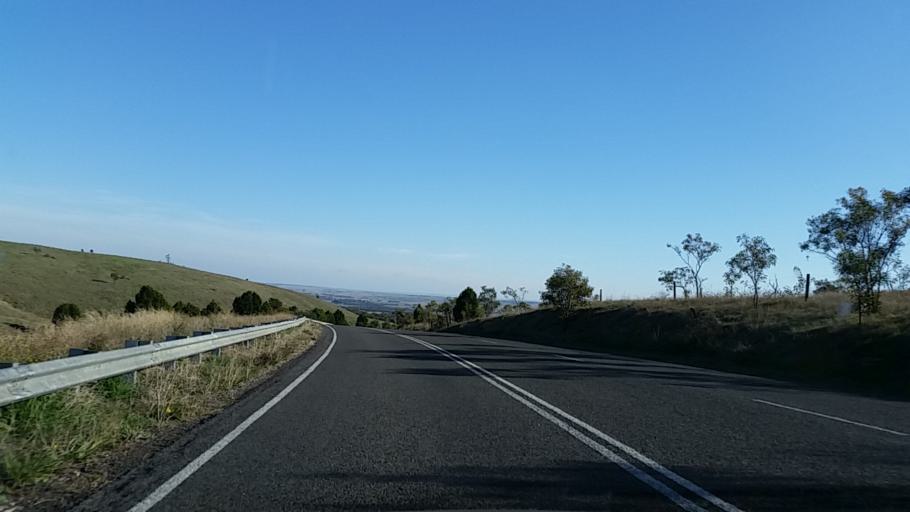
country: AU
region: South Australia
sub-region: Mount Barker
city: Callington
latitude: -35.1126
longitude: 139.0717
